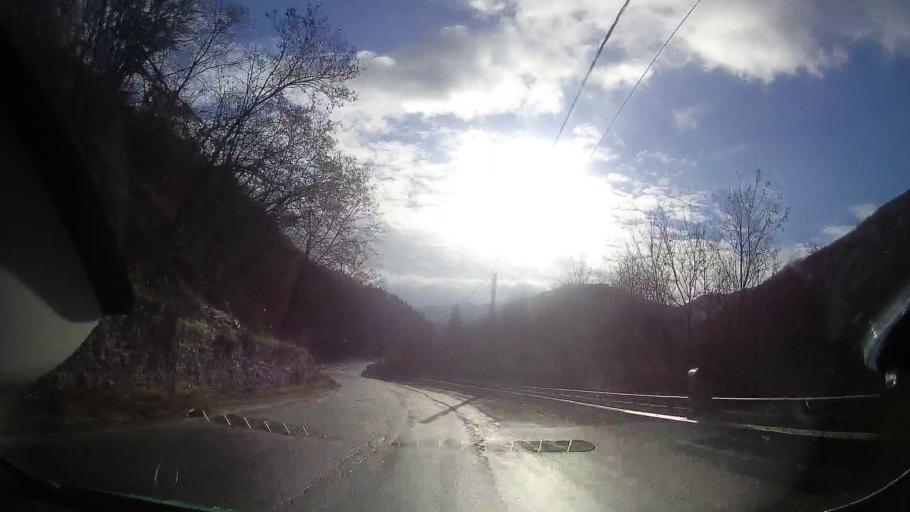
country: RO
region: Alba
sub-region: Comuna Sohodol
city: Sohodol
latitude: 46.3786
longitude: 23.0144
